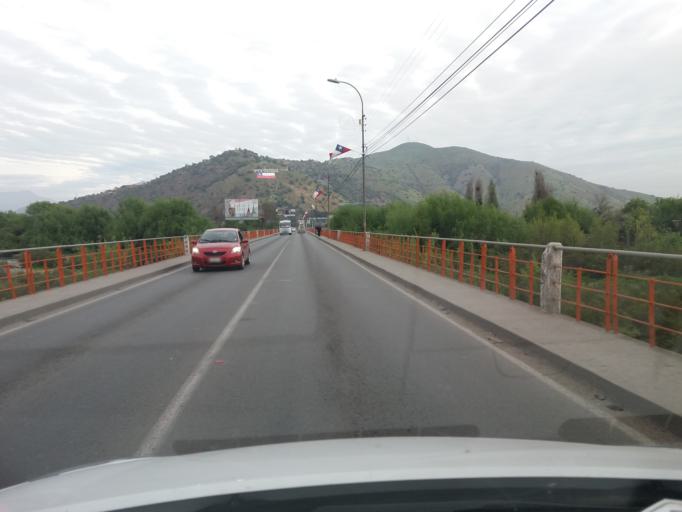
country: CL
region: Valparaiso
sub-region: Provincia de Quillota
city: Hacienda La Calera
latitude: -32.7800
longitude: -71.1912
